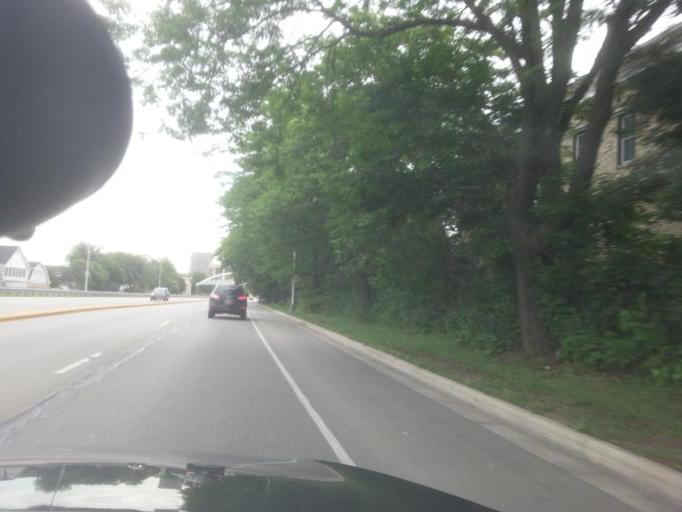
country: US
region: Wisconsin
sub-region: Dane County
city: Madison
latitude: 43.0739
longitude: -89.4205
